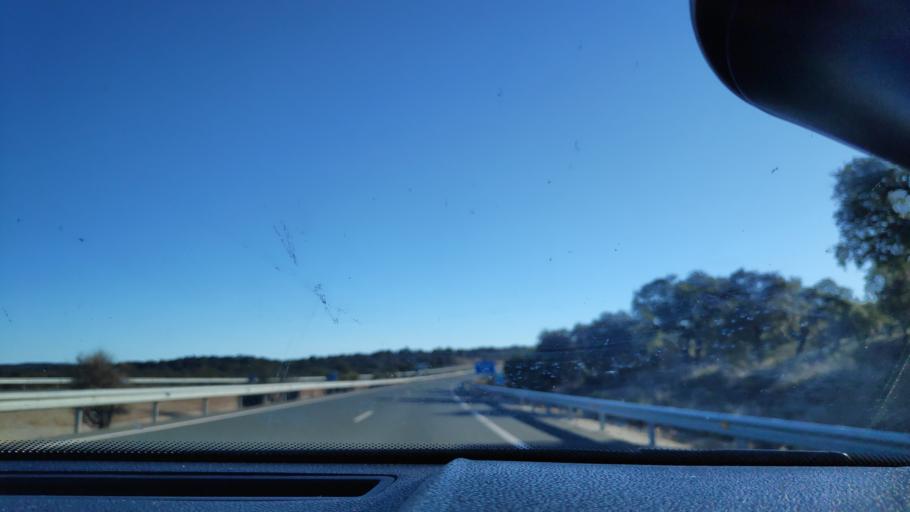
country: ES
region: Andalusia
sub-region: Provincia de Huelva
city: Santa Olalla del Cala
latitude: 37.9412
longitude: -6.2274
